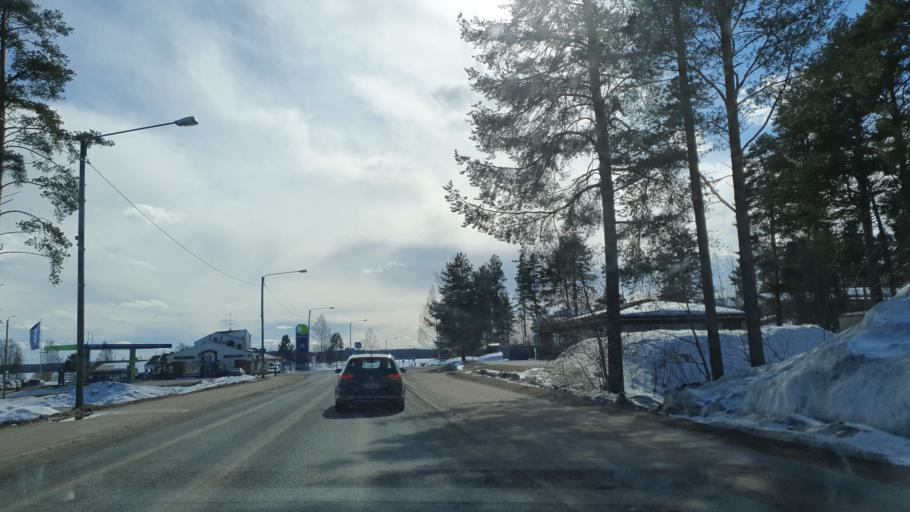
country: FI
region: Kainuu
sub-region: Kajaani
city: Paltamo
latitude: 64.4058
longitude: 27.8388
